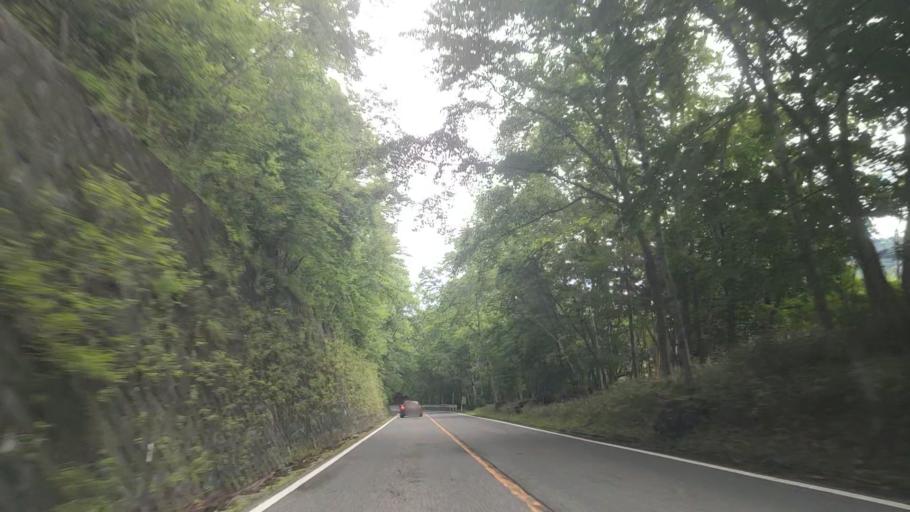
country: JP
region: Tochigi
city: Nikko
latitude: 36.8053
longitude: 139.4268
